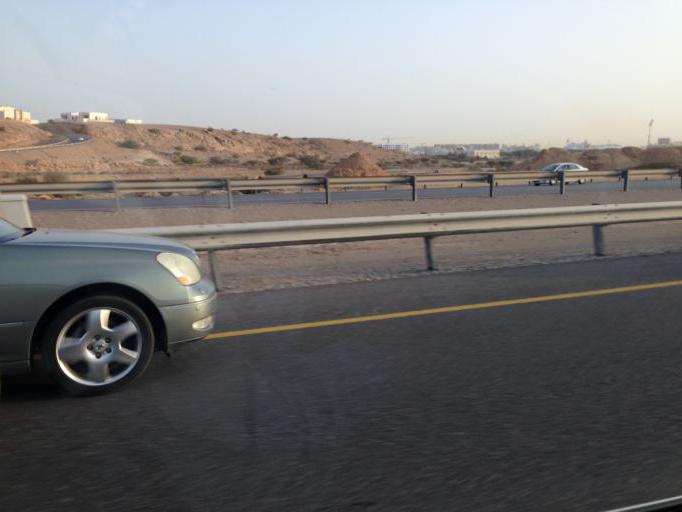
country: OM
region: Muhafazat Masqat
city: Bawshar
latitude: 23.5637
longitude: 58.3918
